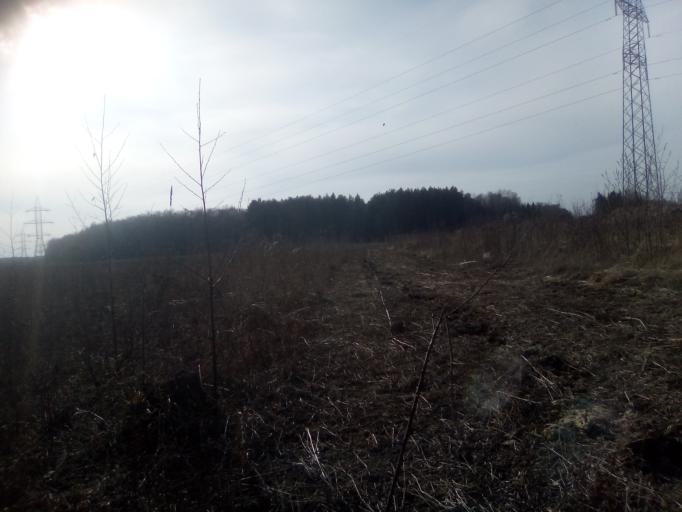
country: RU
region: Moskovskaya
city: Dubrovitsy
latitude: 55.4800
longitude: 37.4429
